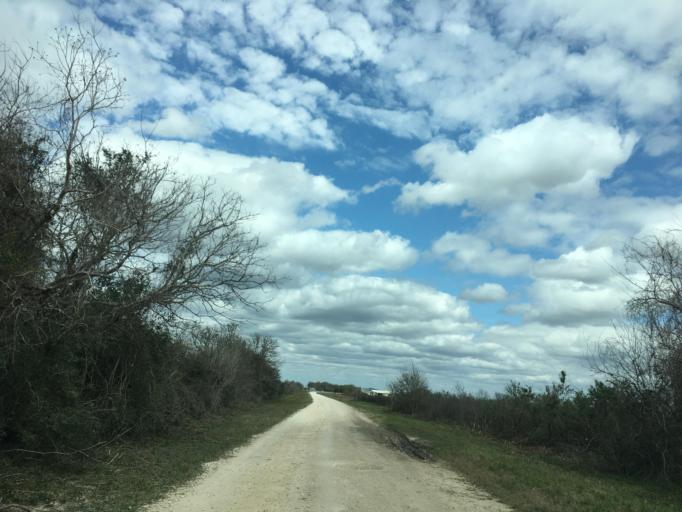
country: US
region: Texas
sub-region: Brazoria County
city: Oyster Creek
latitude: 29.0558
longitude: -95.2687
